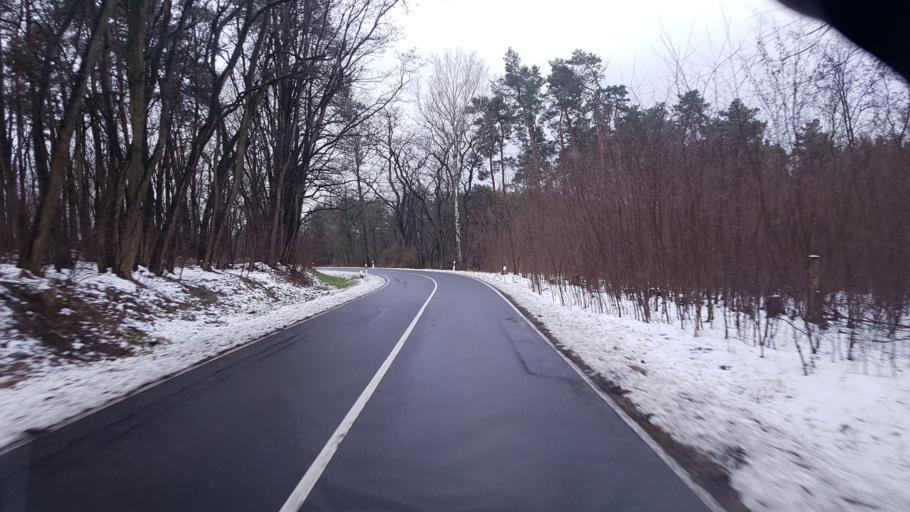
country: DE
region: Brandenburg
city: Schenkendobern
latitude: 51.9159
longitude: 14.6218
